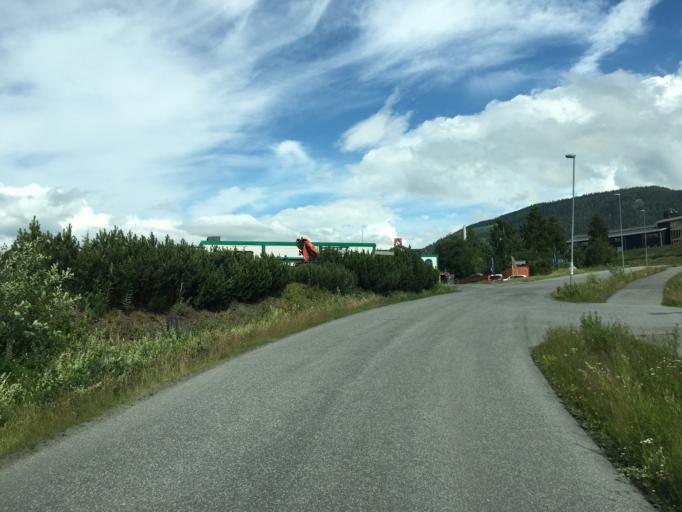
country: NO
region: Oppland
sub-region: Lillehammer
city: Lillehammer
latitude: 61.1285
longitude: 10.4358
